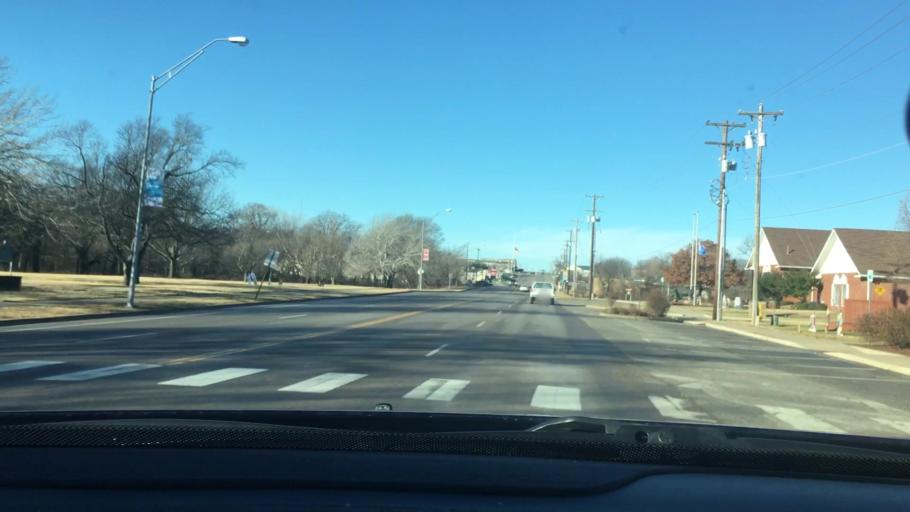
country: US
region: Oklahoma
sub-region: Murray County
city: Sulphur
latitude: 34.5065
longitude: -96.9738
